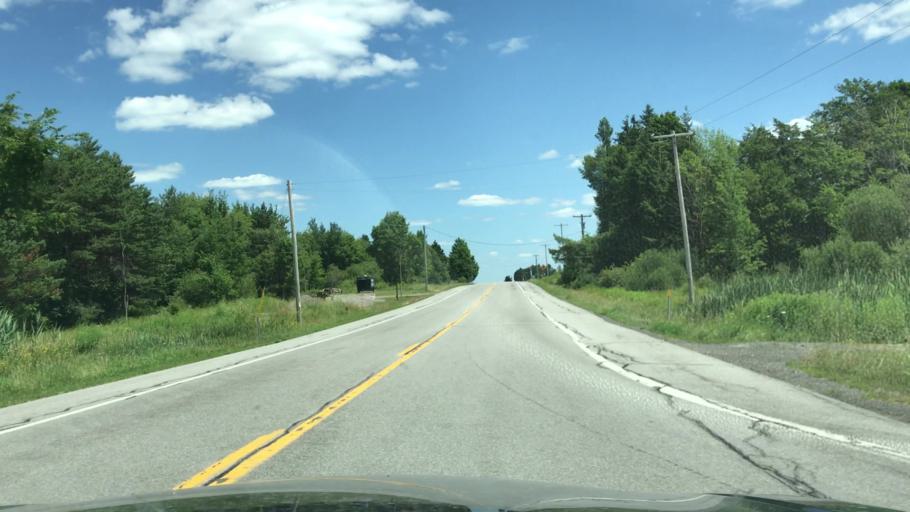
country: US
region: New York
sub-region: Wyoming County
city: Warsaw
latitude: 42.7461
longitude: -78.2241
